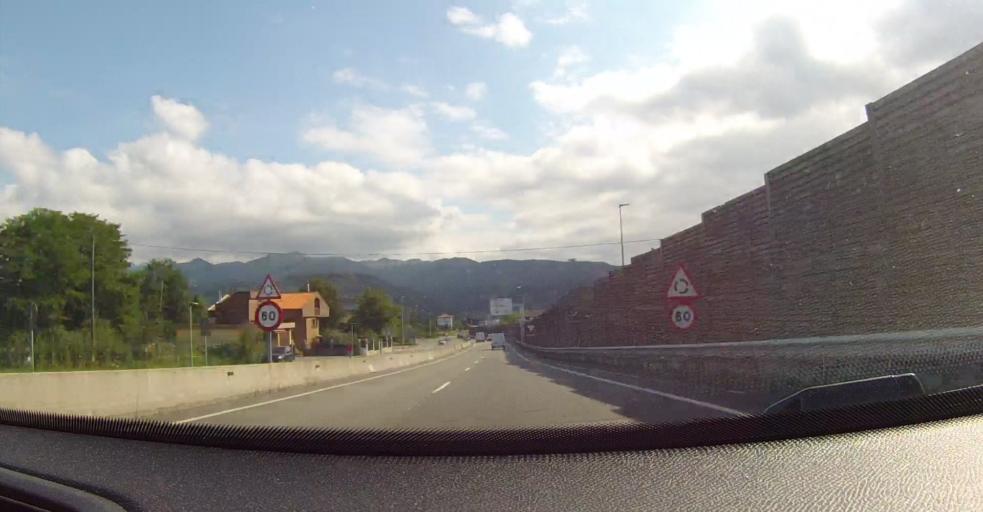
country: ES
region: Basque Country
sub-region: Bizkaia
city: Amorebieta
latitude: 43.2286
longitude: -2.7300
